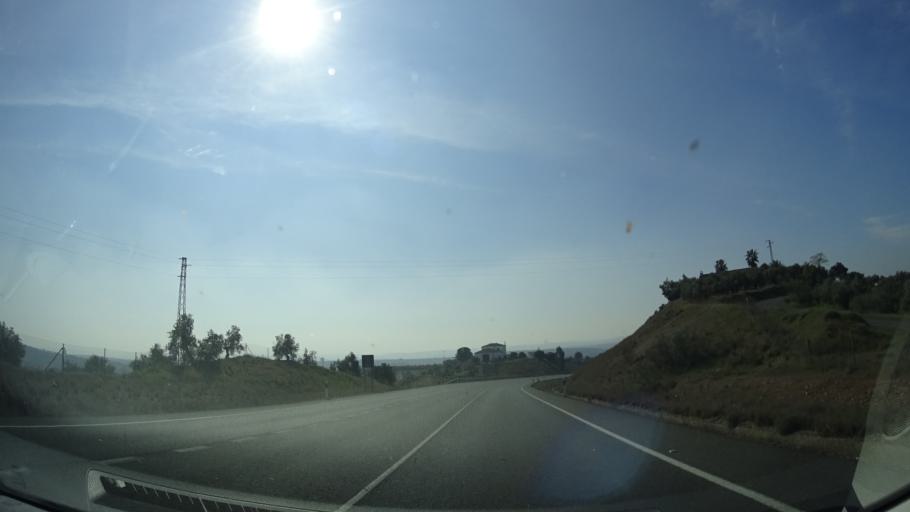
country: ES
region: Andalusia
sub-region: Province of Cordoba
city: Montoro
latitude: 38.0332
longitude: -4.3703
